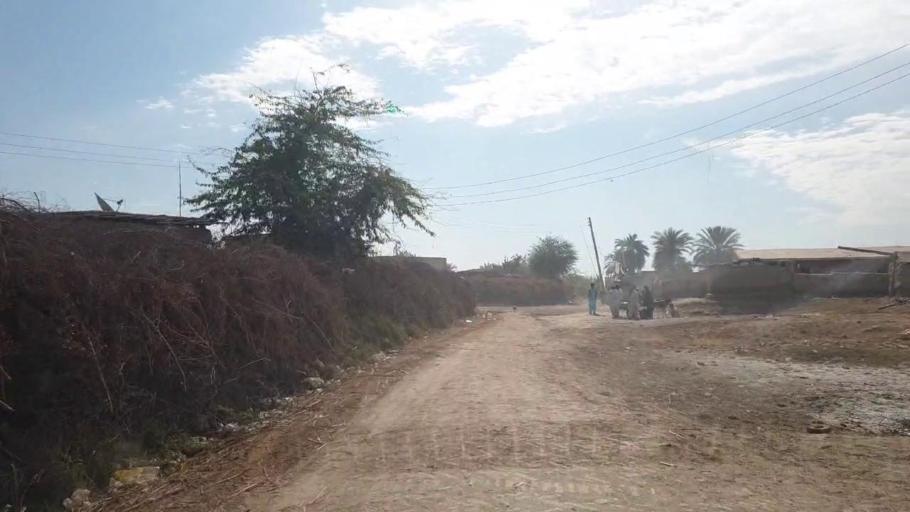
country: PK
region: Sindh
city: Sanghar
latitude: 26.0342
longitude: 68.9181
